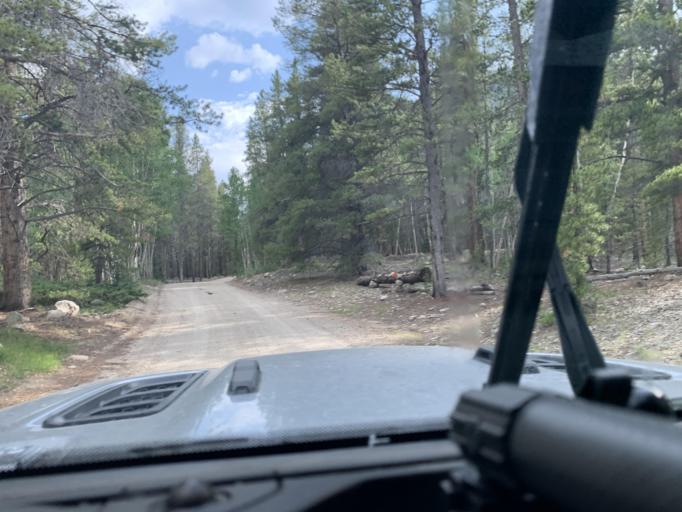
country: US
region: Colorado
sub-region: Chaffee County
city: Buena Vista
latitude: 38.7021
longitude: -106.3502
